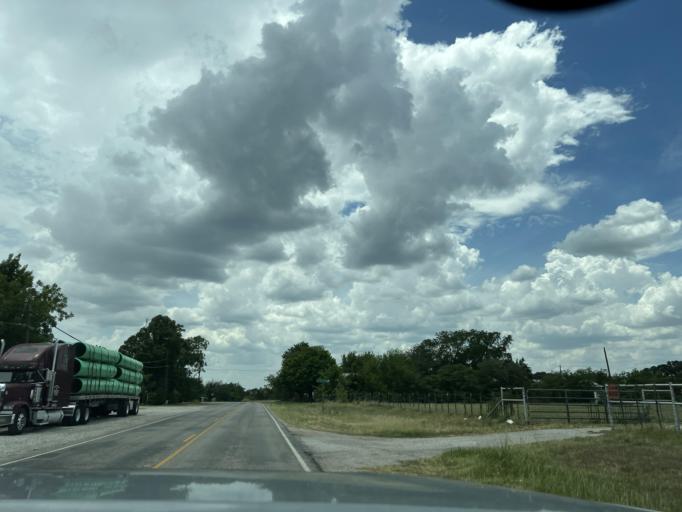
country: US
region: Texas
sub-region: Eastland County
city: Eastland
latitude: 32.4193
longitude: -98.7555
